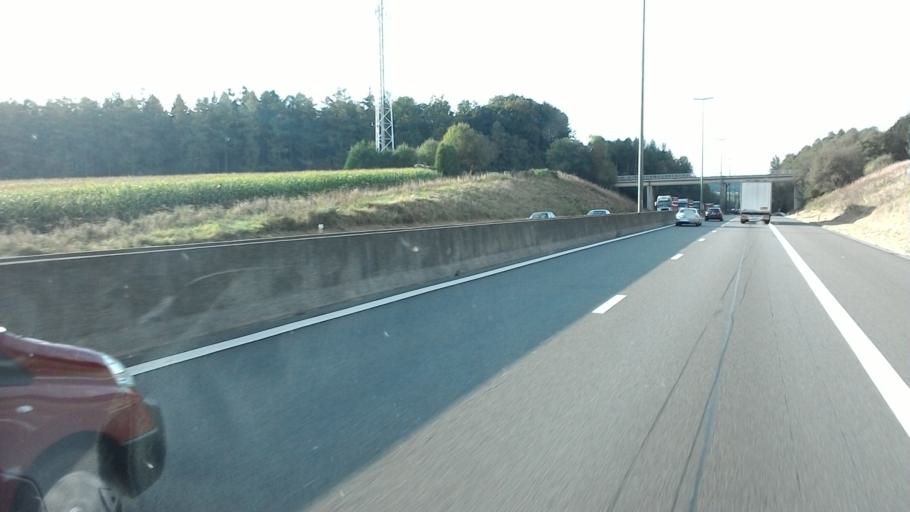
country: BE
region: Wallonia
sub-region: Province du Luxembourg
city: Leglise
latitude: 49.7835
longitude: 5.5359
